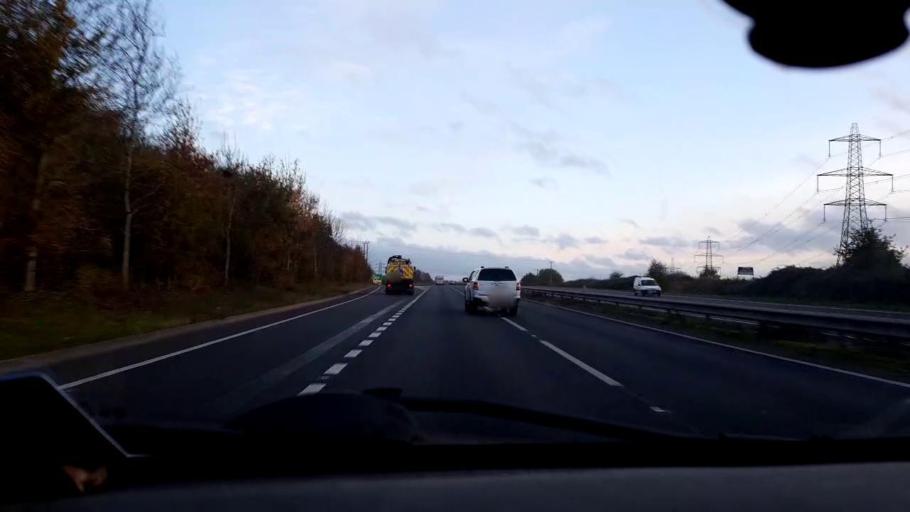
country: GB
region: England
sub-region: Norfolk
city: Cringleford
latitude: 52.6075
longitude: 1.2203
